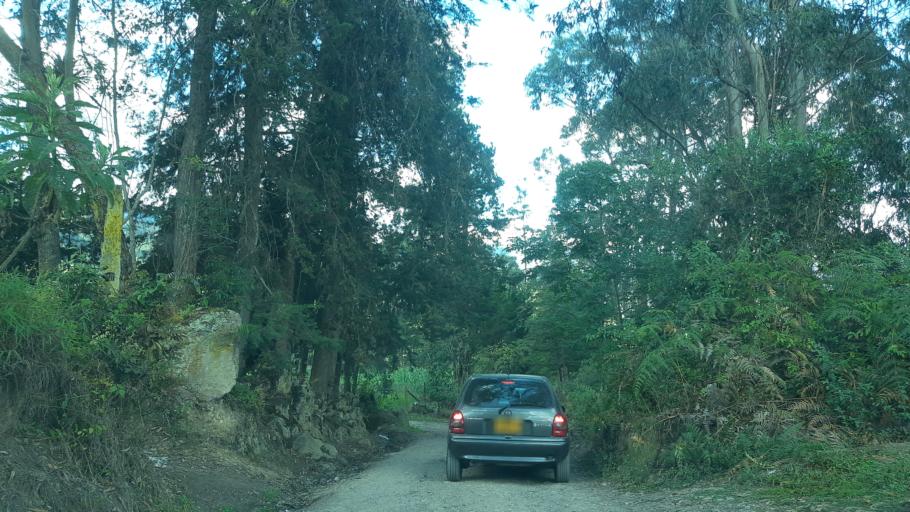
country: CO
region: Cundinamarca
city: Macheta
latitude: 5.0724
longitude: -73.6209
